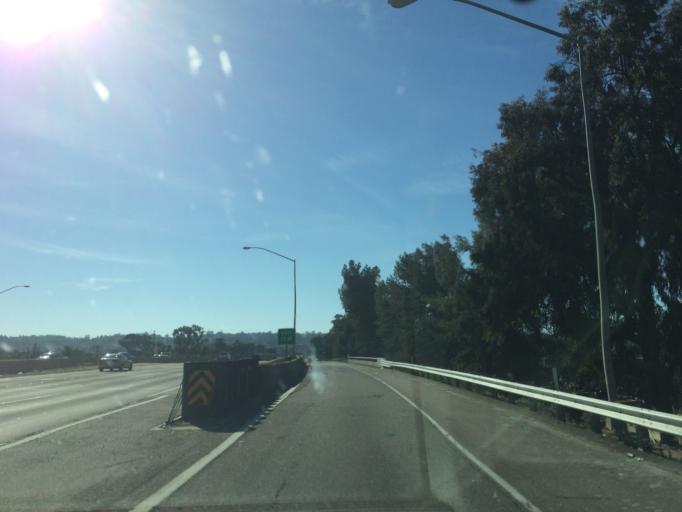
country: US
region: California
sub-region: San Diego County
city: El Cajon
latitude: 32.8033
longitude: -116.9571
